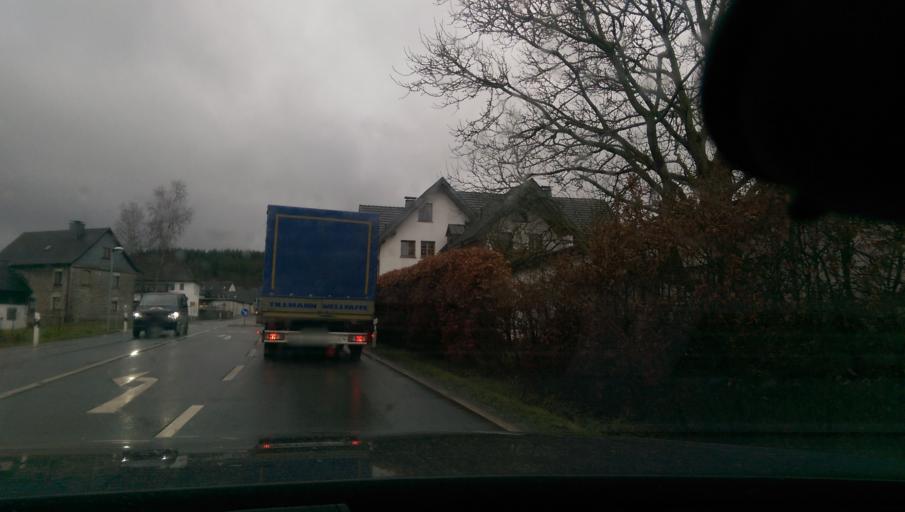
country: DE
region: North Rhine-Westphalia
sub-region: Regierungsbezirk Arnsberg
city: Sundern
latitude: 51.2971
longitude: 7.9838
